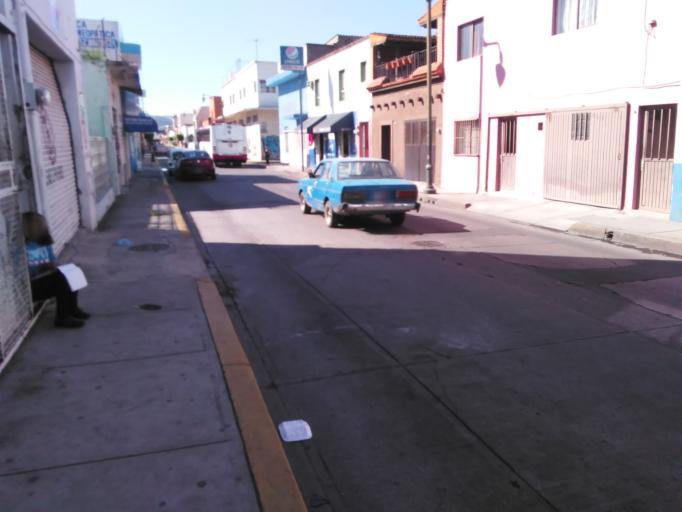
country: MX
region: Nayarit
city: Tepic
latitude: 21.5120
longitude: -104.8892
